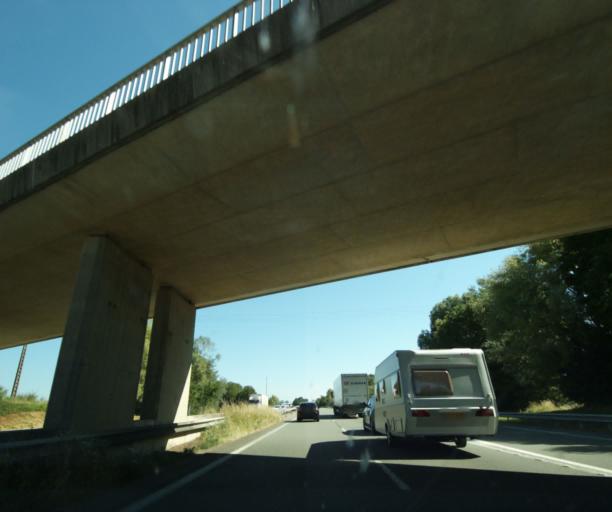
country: FR
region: Champagne-Ardenne
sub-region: Departement de la Haute-Marne
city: Avrecourt
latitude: 47.9923
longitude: 5.5122
